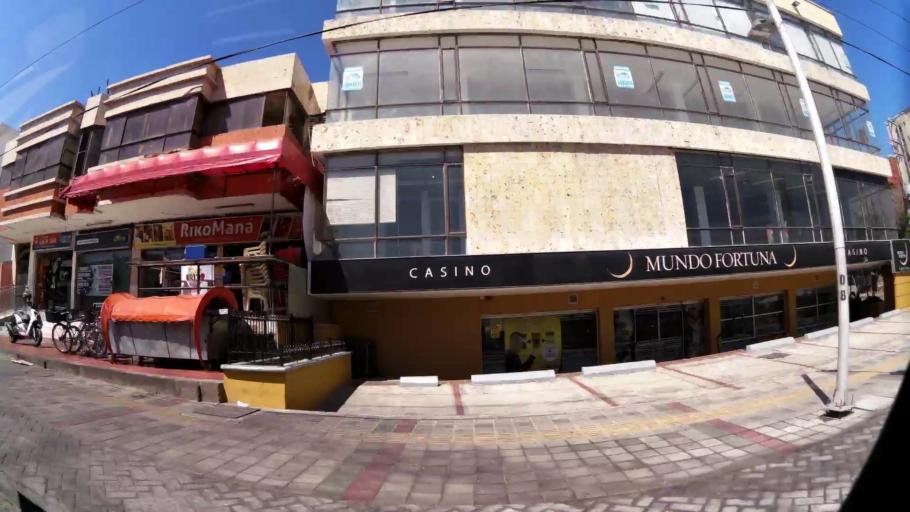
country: CO
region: Atlantico
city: Barranquilla
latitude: 11.0040
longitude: -74.8083
